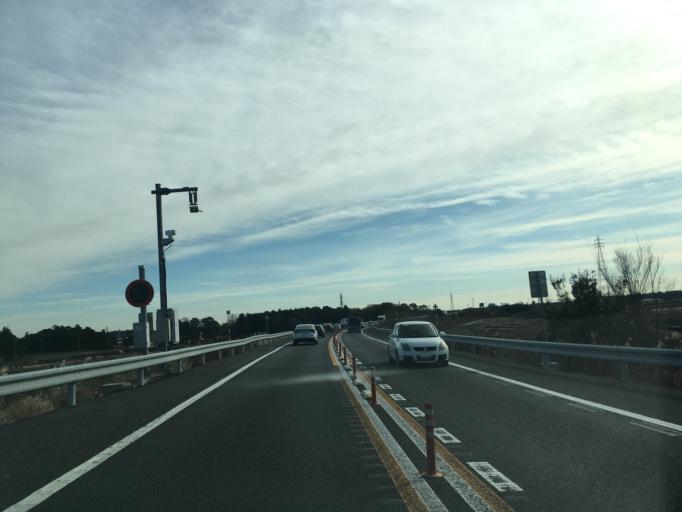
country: JP
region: Ibaraki
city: Naka
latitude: 36.0526
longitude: 140.1027
